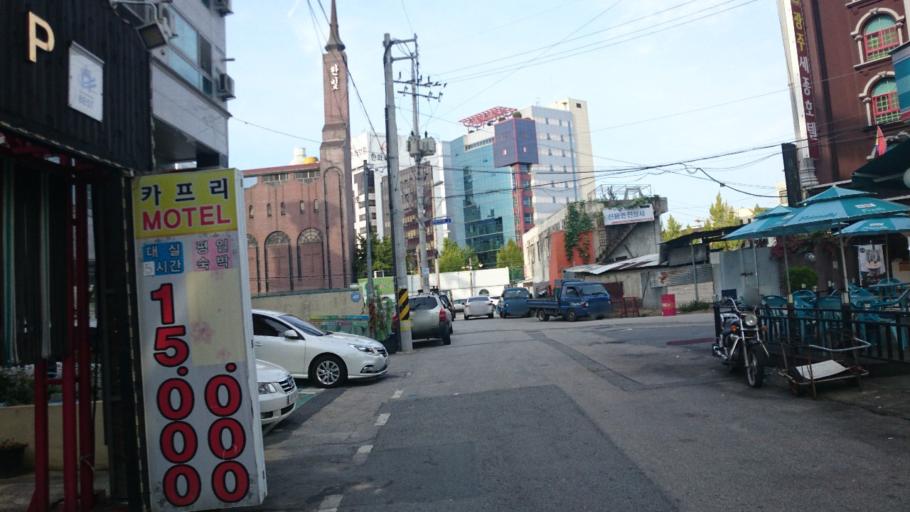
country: KR
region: Gwangju
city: Gwangju
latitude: 35.1618
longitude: 126.9088
